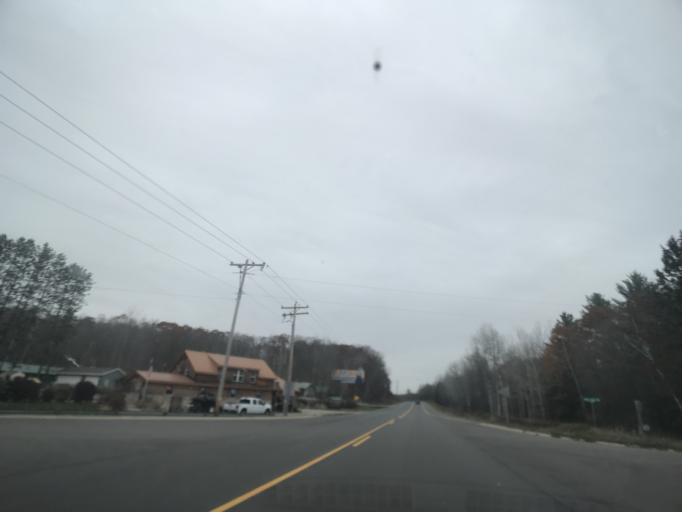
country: US
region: Wisconsin
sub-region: Menominee County
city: Legend Lake
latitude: 45.2841
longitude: -88.5101
